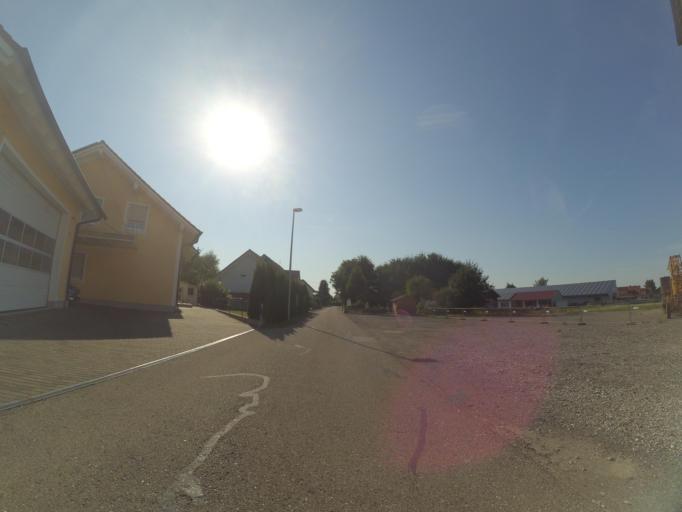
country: DE
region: Bavaria
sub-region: Swabia
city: Dirlewang
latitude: 48.0019
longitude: 10.5089
